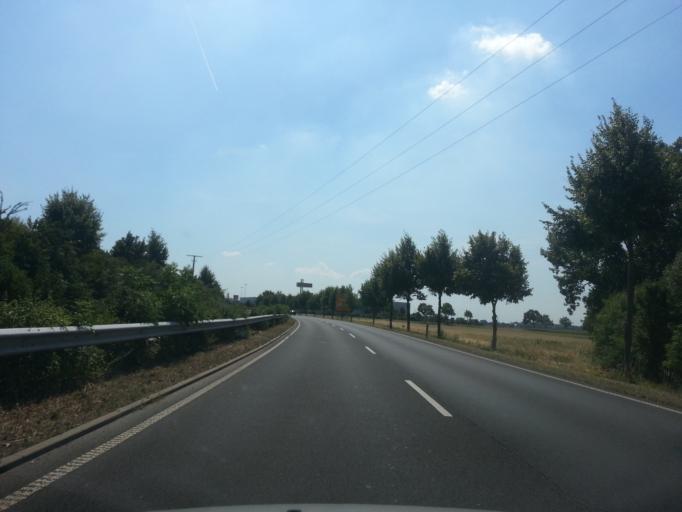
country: DE
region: Hesse
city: Lampertheim
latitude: 49.5626
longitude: 8.4454
